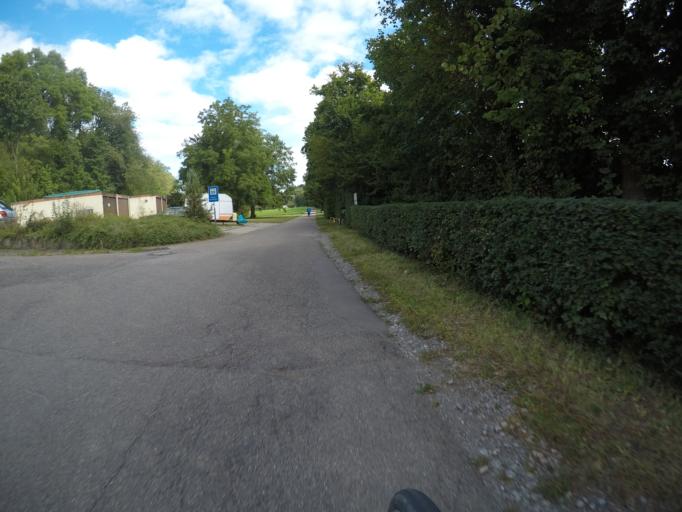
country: DE
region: Baden-Wuerttemberg
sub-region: Regierungsbezirk Stuttgart
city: Marbach am Neckar
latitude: 48.9382
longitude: 9.2501
